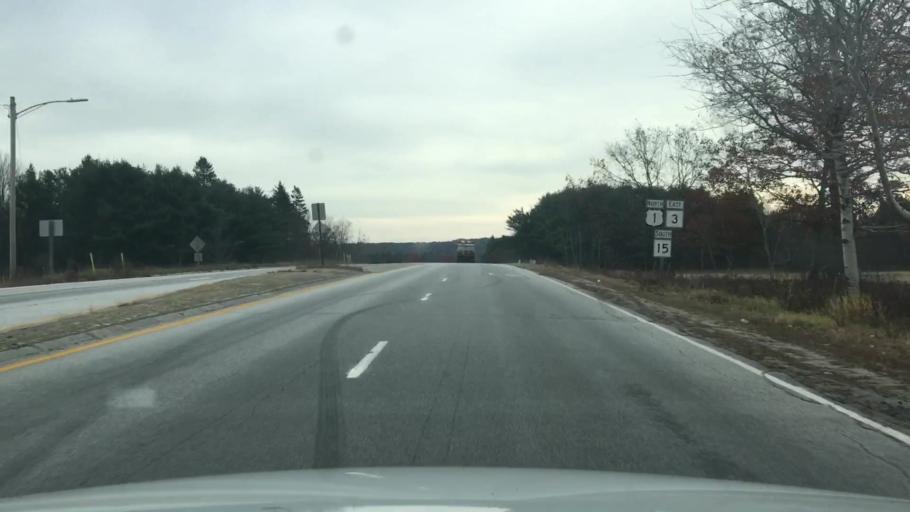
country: US
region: Maine
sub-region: Hancock County
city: Orland
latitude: 44.5733
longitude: -68.7305
